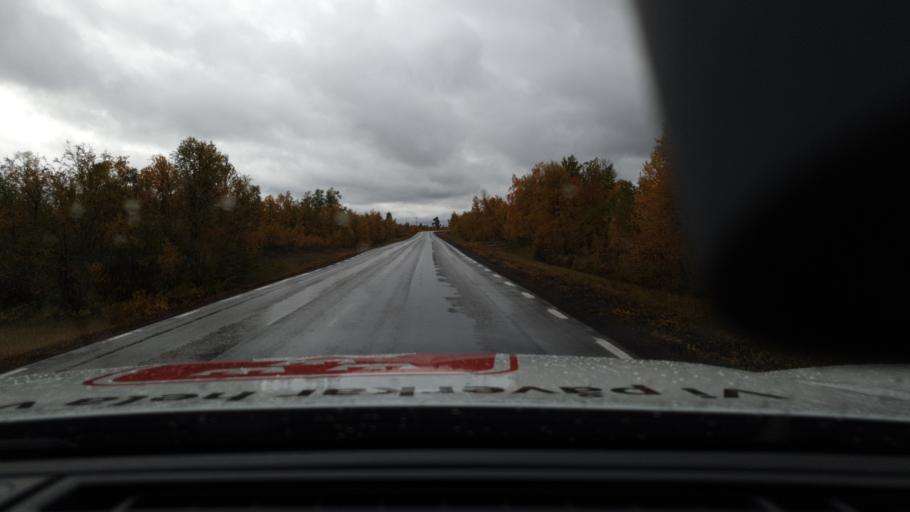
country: SE
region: Norrbotten
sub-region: Kiruna Kommun
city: Kiruna
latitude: 67.7842
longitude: 20.2275
